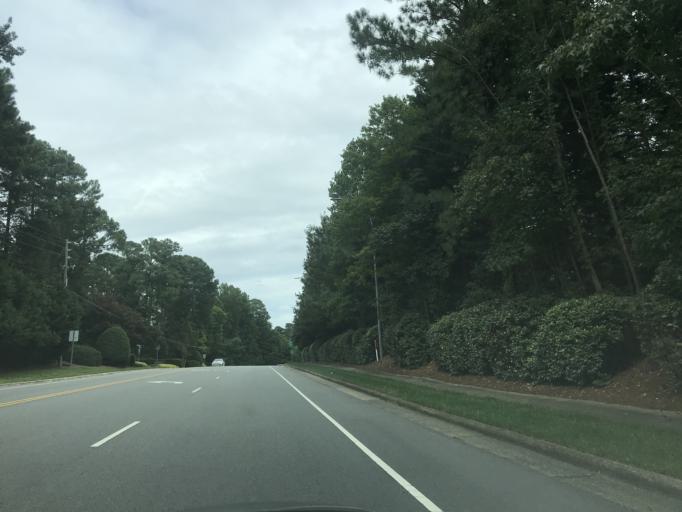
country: US
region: North Carolina
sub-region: Wake County
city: Apex
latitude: 35.7496
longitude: -78.8137
